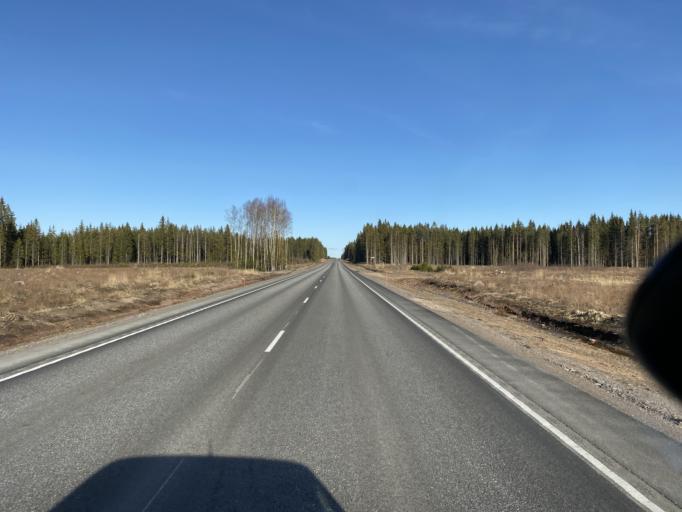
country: FI
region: Satakunta
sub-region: Rauma
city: Koeylioe
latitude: 61.1631
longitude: 22.3327
